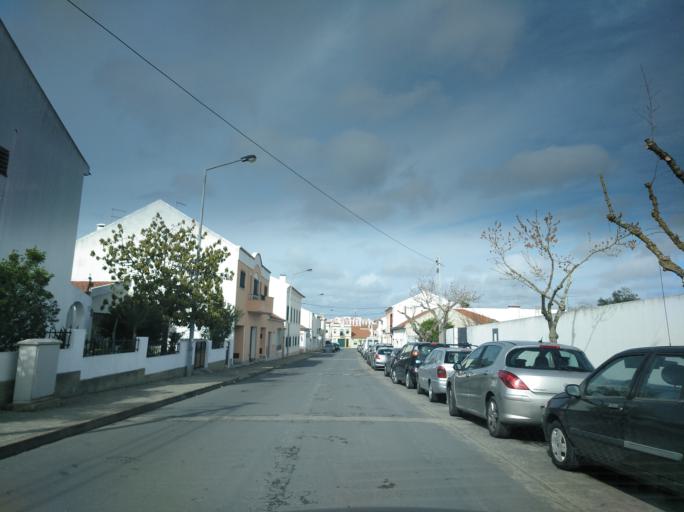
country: PT
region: Setubal
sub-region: Grandola
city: Grandola
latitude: 38.1758
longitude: -8.5613
